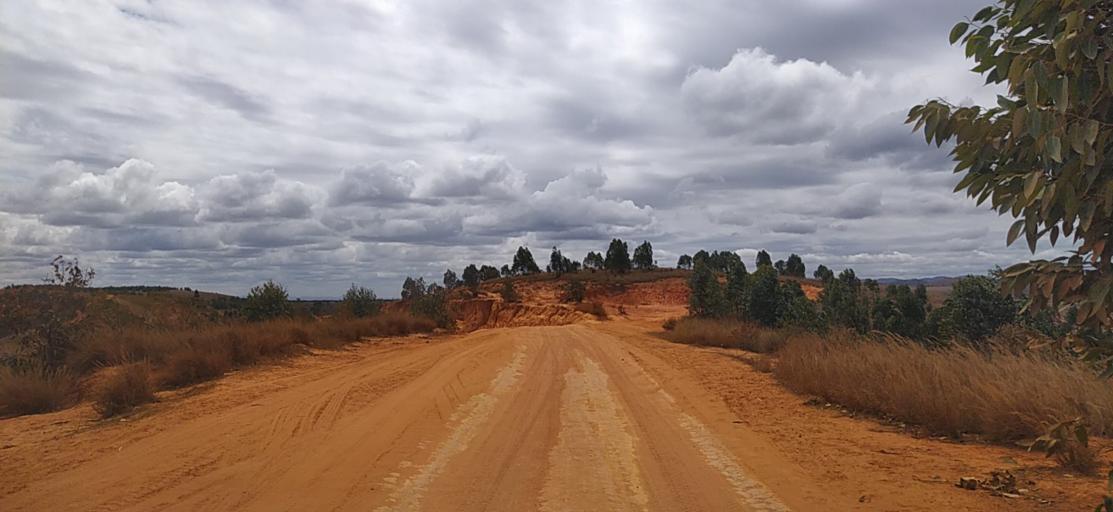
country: MG
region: Alaotra Mangoro
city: Ambatondrazaka
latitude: -18.0619
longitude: 48.2571
